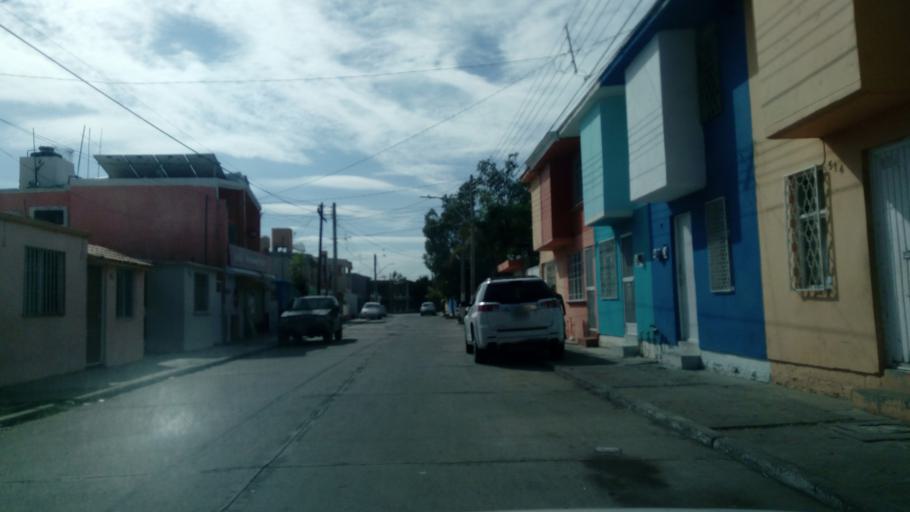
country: MX
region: Durango
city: Victoria de Durango
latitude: 24.0074
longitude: -104.6554
